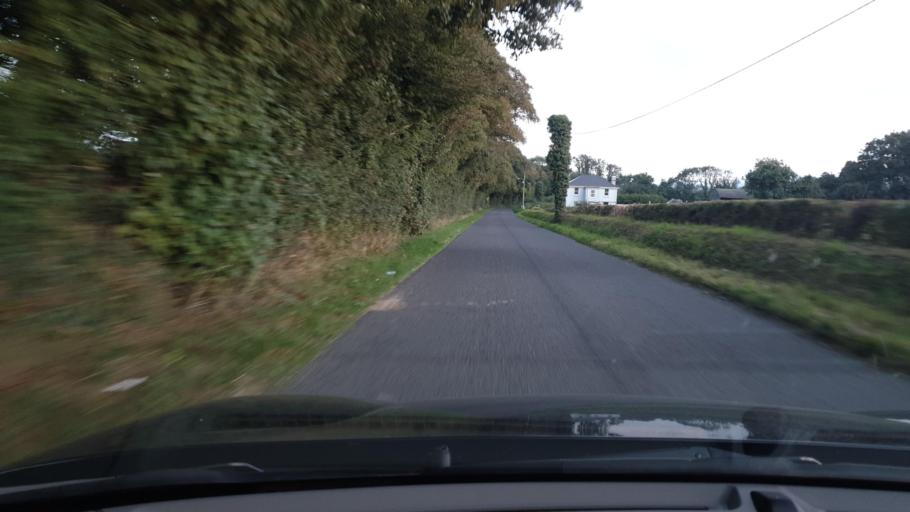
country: IE
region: Leinster
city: Balrothery
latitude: 53.5718
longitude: -6.1553
